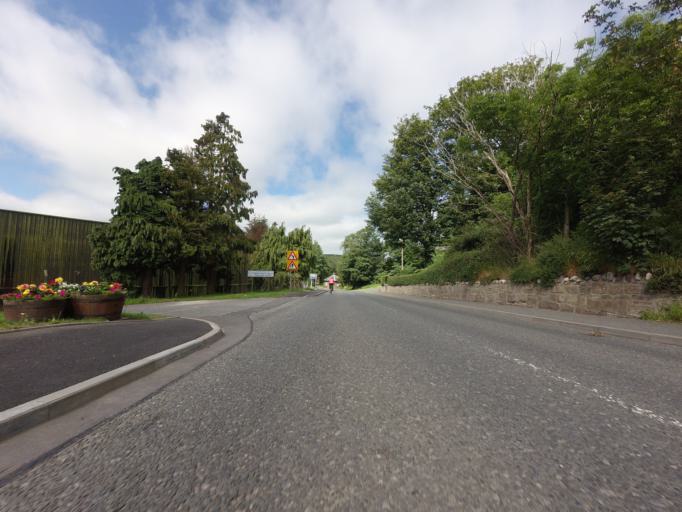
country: GB
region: Scotland
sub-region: Aberdeenshire
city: Turriff
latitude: 57.5424
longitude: -2.4766
